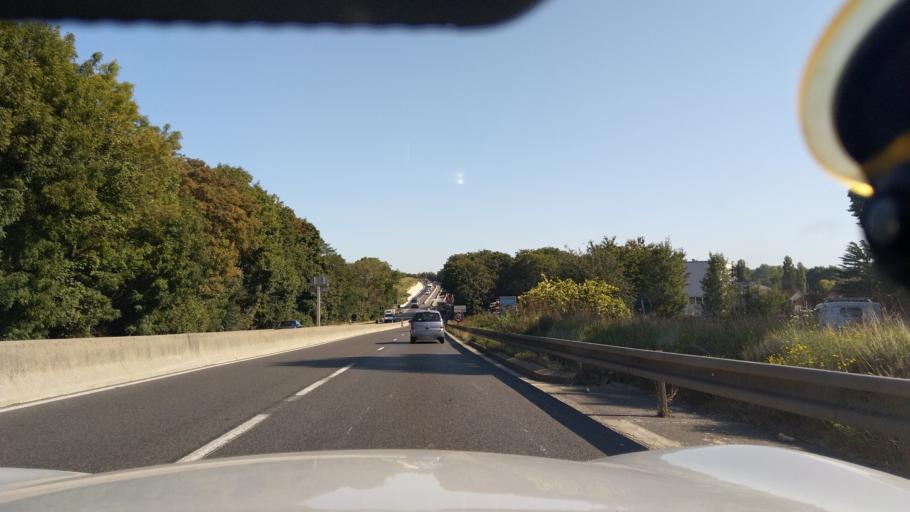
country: FR
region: Ile-de-France
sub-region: Departement du Val-d'Oise
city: Le Thillay
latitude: 48.9996
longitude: 2.4838
